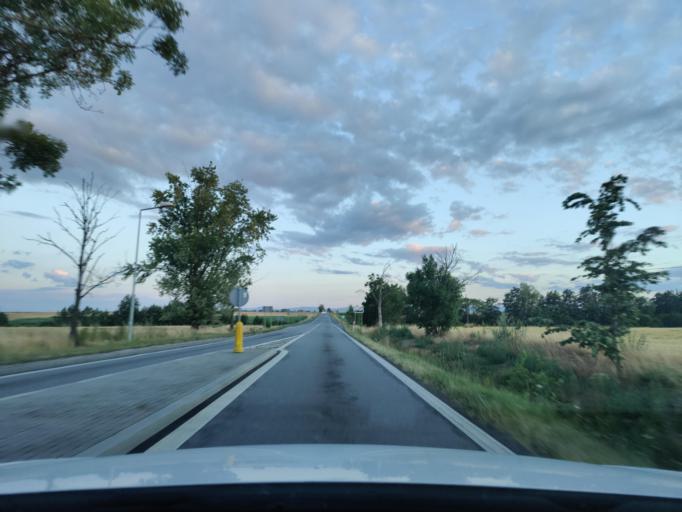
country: PL
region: Opole Voivodeship
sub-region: Powiat nyski
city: Skoroszyce
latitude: 50.5932
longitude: 17.3822
